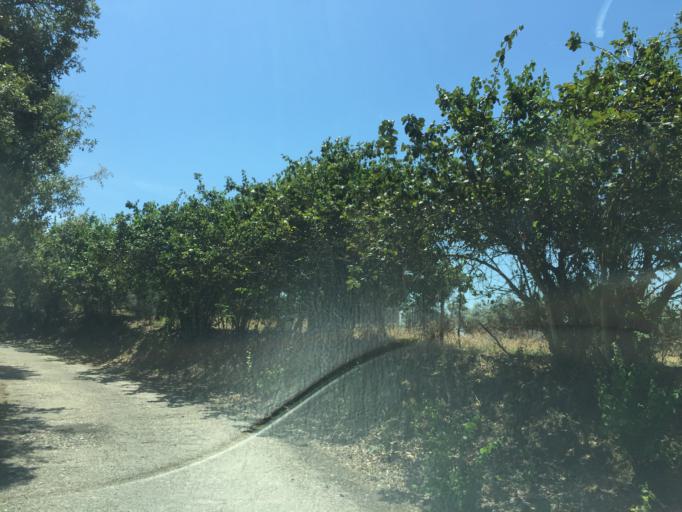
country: PT
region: Santarem
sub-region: Tomar
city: Tomar
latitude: 39.5964
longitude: -8.3533
